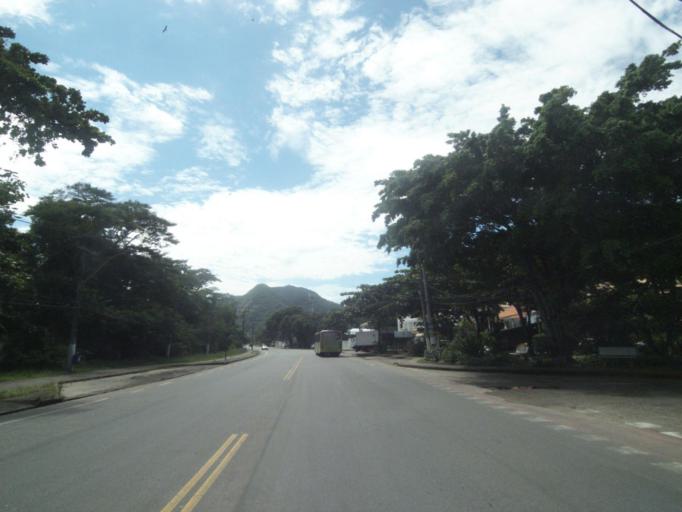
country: BR
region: Rio de Janeiro
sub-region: Niteroi
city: Niteroi
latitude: -22.9665
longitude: -43.0376
